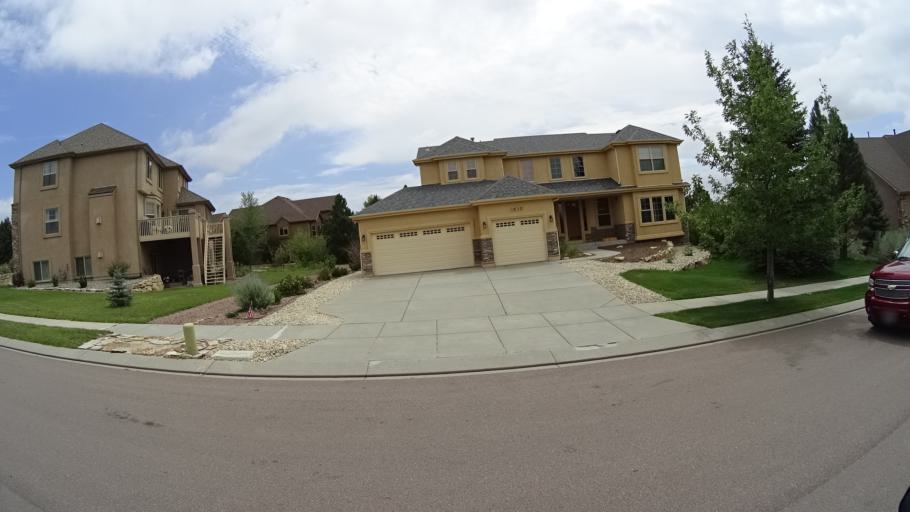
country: US
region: Colorado
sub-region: El Paso County
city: Gleneagle
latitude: 39.0155
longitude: -104.7967
